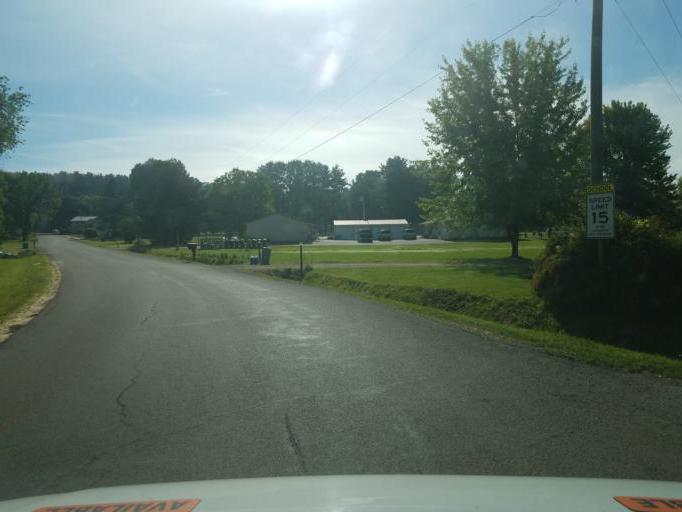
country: US
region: Wisconsin
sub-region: Sauk County
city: Reedsburg
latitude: 43.5787
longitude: -90.1373
